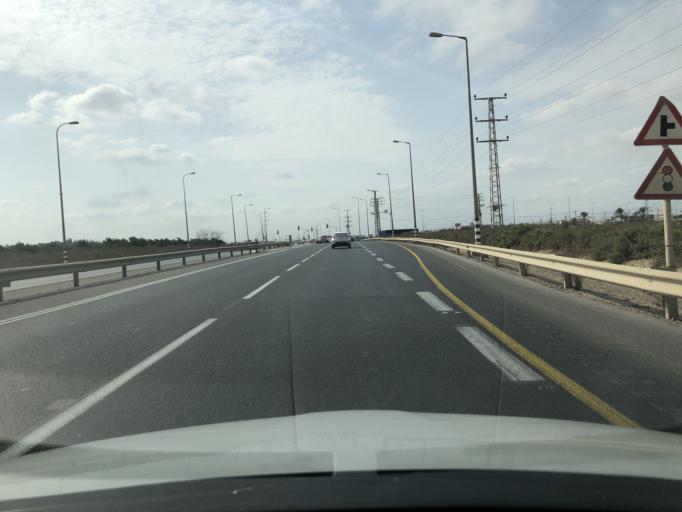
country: IL
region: Central District
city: Tirah
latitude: 32.2339
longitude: 34.9853
